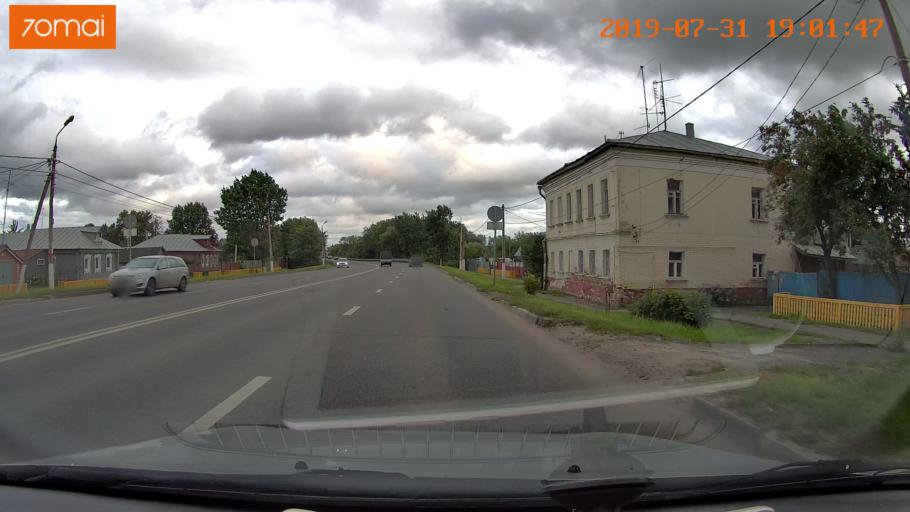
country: RU
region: Moskovskaya
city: Raduzhnyy
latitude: 55.1241
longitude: 38.7294
